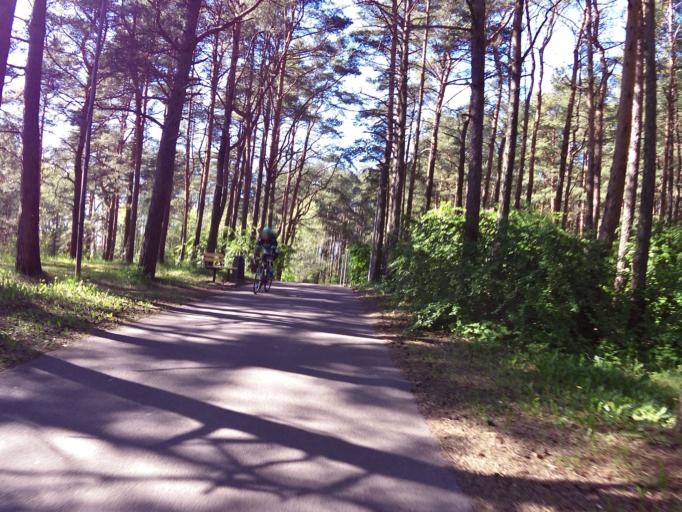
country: EE
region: Harju
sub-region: Viimsi vald
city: Viimsi
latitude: 59.4682
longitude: 24.8316
